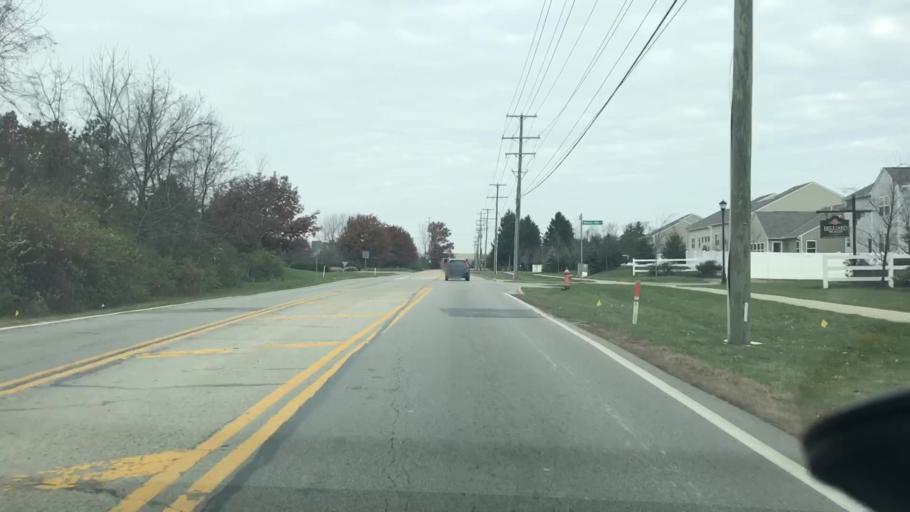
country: US
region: Ohio
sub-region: Franklin County
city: Lincoln Village
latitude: 39.9951
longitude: -83.1136
